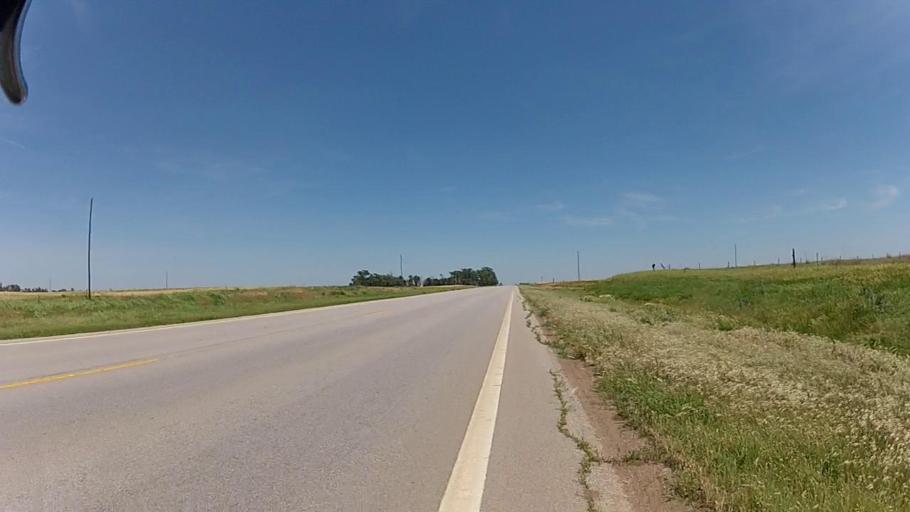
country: US
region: Kansas
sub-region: Harper County
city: Harper
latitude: 37.2386
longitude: -98.1136
